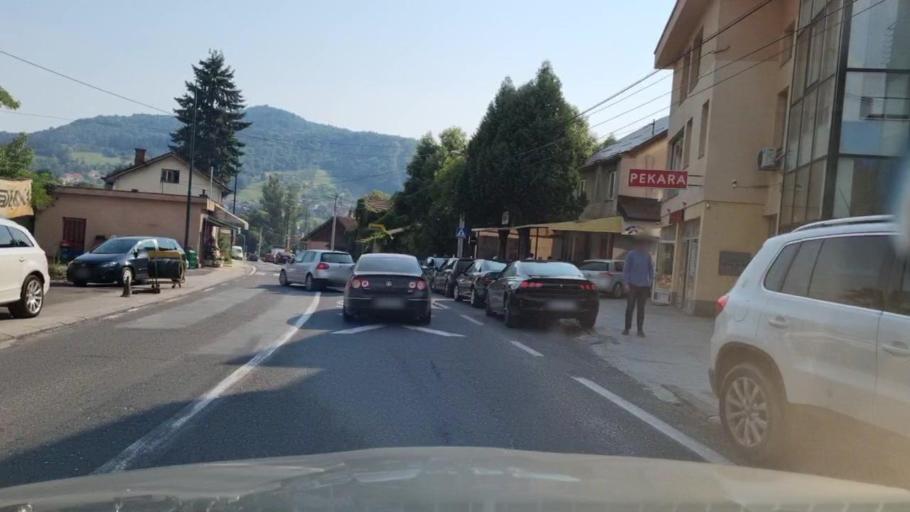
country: BA
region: Federation of Bosnia and Herzegovina
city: Vogosca
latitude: 43.9228
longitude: 18.3177
